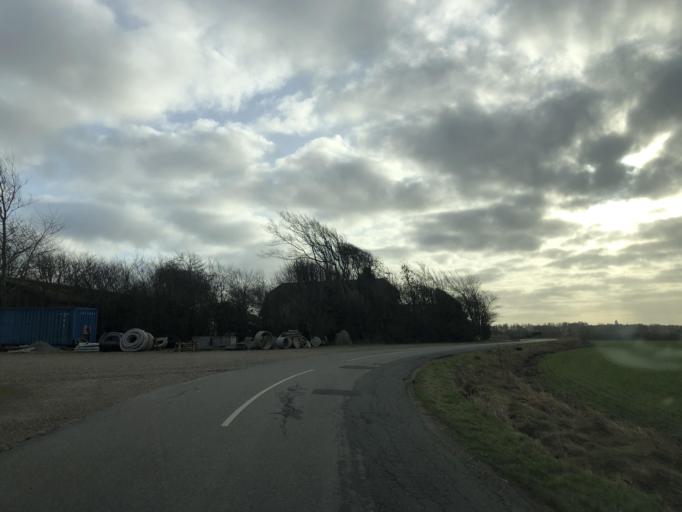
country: DK
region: Central Jutland
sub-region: Holstebro Kommune
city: Ulfborg
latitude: 56.4024
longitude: 8.3573
